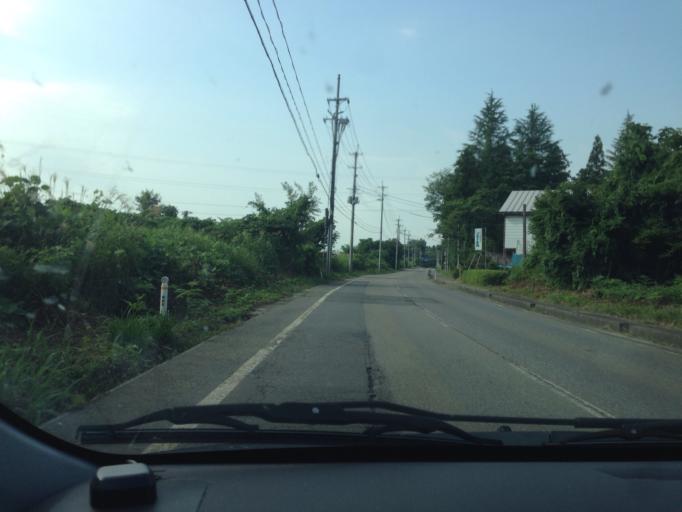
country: JP
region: Fukushima
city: Kitakata
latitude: 37.7074
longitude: 139.8782
